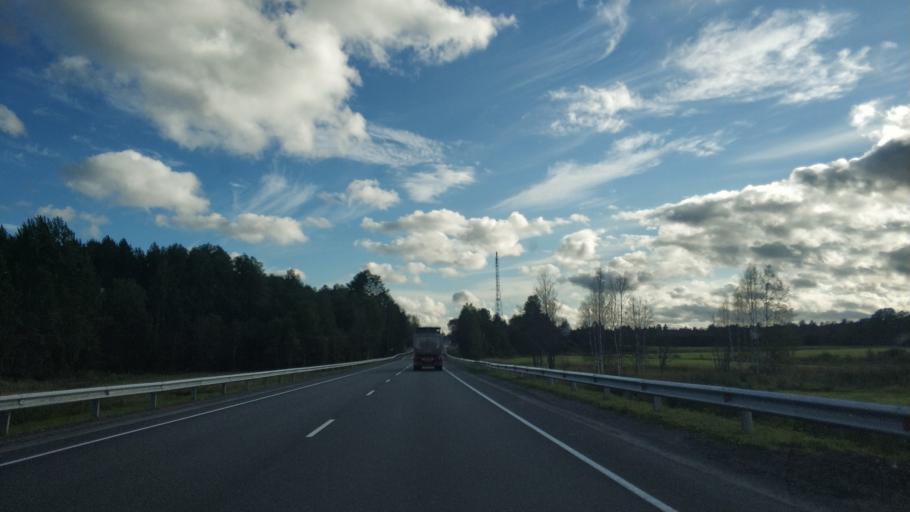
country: RU
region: Leningrad
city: Priozersk
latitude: 60.8563
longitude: 30.1536
